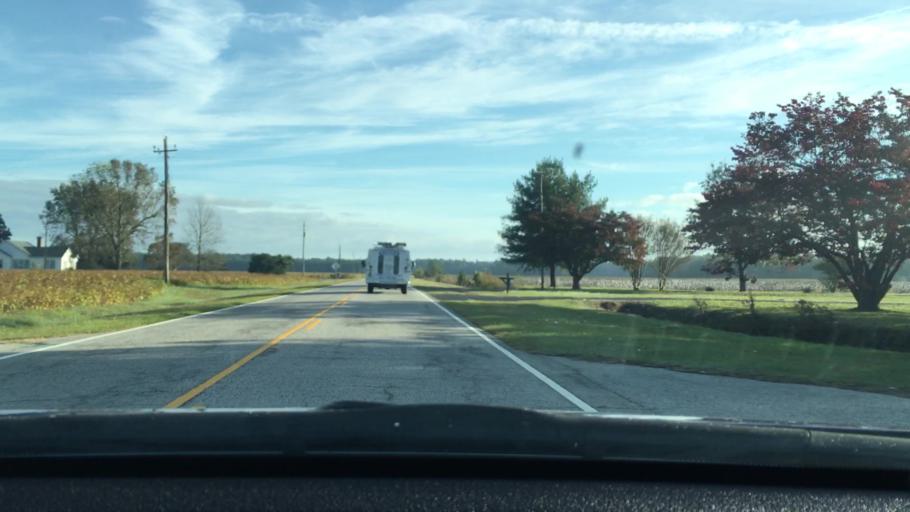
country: US
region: South Carolina
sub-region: Lee County
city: Bishopville
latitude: 34.0794
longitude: -80.1989
